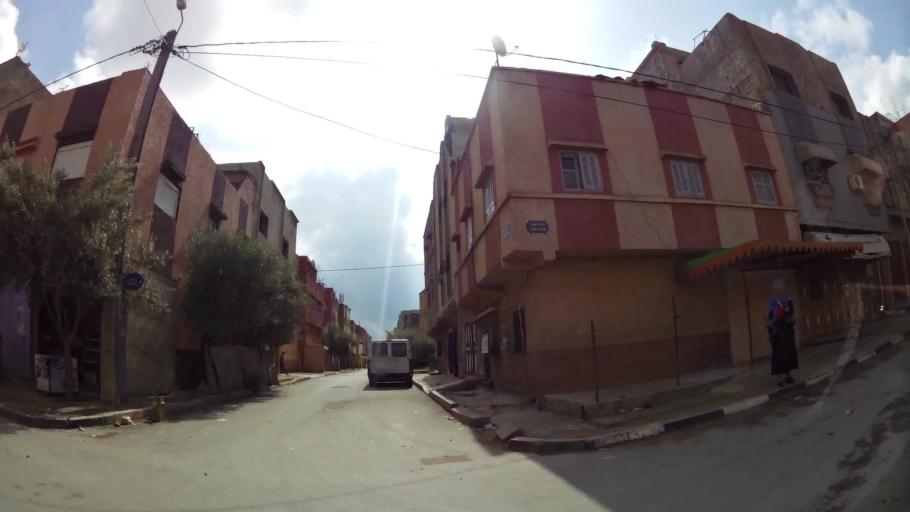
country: MA
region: Rabat-Sale-Zemmour-Zaer
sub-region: Khemisset
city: Tiflet
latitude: 33.8963
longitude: -6.3215
